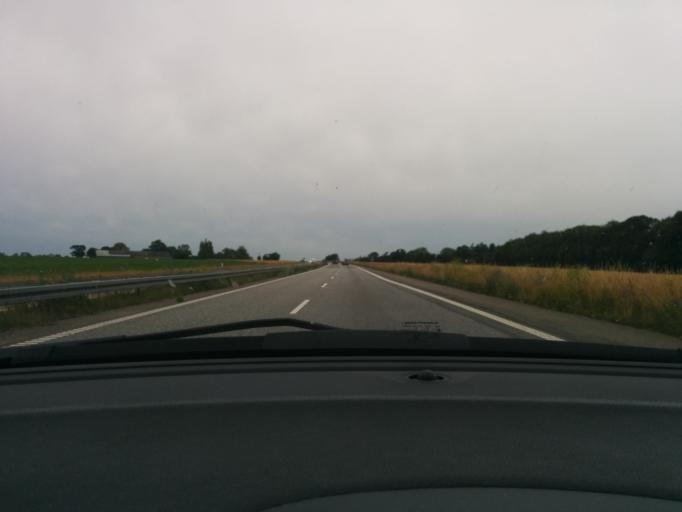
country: DK
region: Zealand
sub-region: Guldborgsund Kommune
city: Sakskobing
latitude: 54.8173
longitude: 11.6977
